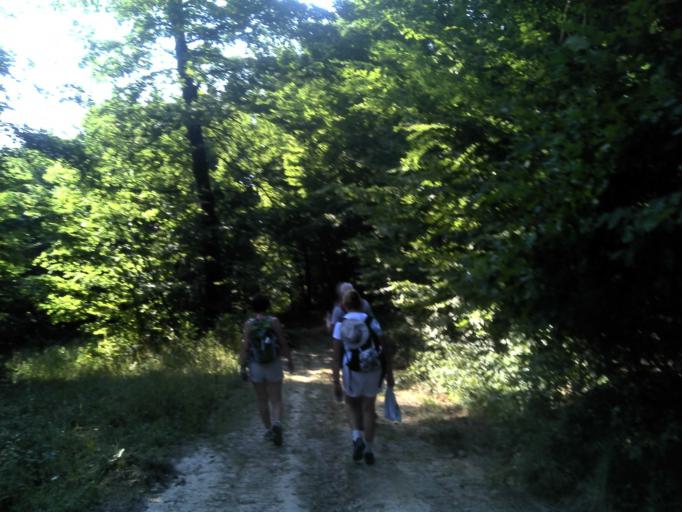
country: HU
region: Baranya
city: Pellerd
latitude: 46.1329
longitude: 18.1276
